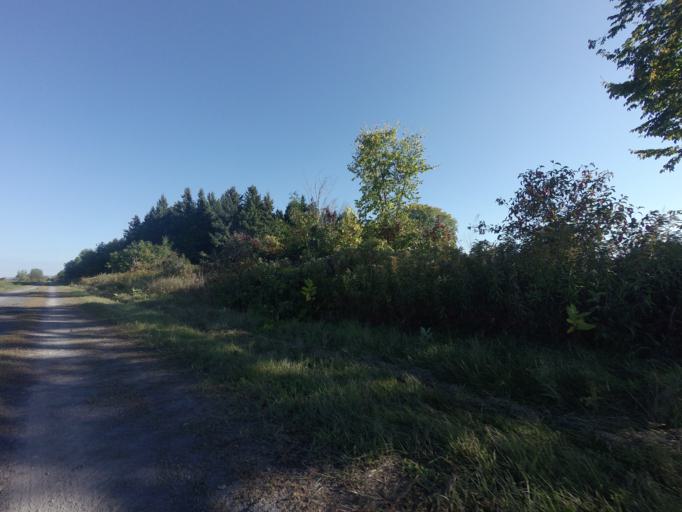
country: CA
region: Ontario
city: Hawkesbury
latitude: 45.5190
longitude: -74.5274
